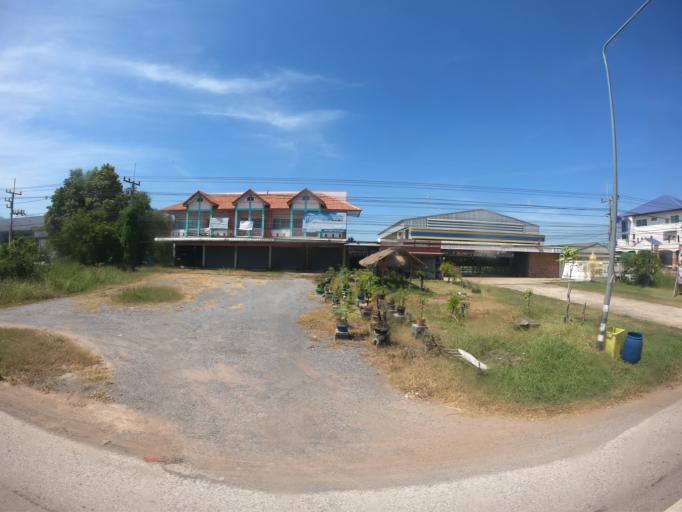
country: TH
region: Nakhon Ratchasima
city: Sida
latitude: 15.5447
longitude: 102.5472
